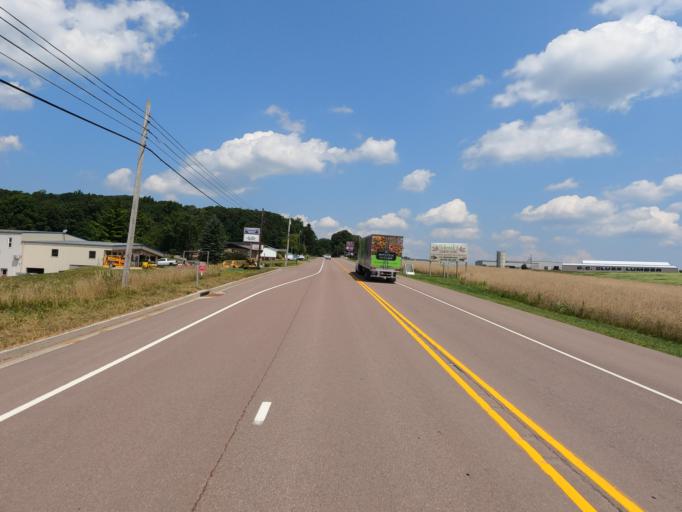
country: US
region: Maryland
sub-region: Garrett County
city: Mountain Lake Park
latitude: 39.4425
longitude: -79.3781
